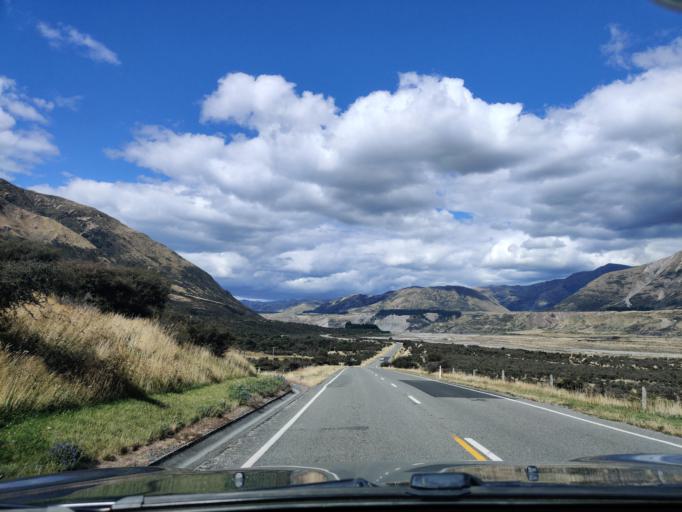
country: NZ
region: Canterbury
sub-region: Hurunui District
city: Amberley
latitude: -42.5821
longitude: 172.3812
